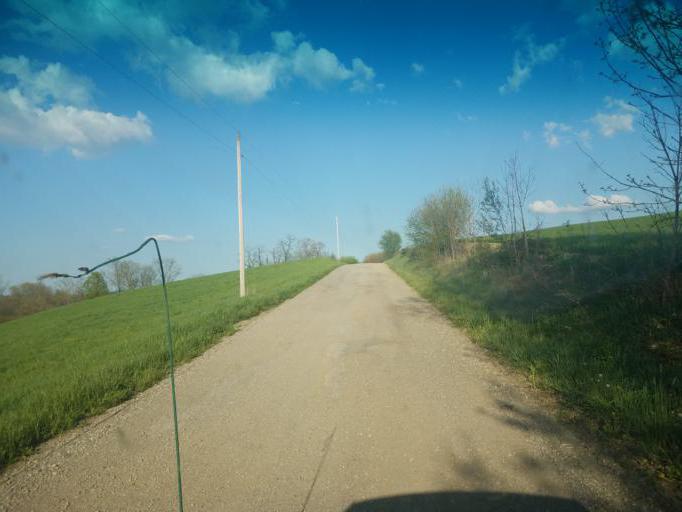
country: US
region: Ohio
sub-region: Wayne County
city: Shreve
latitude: 40.5950
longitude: -82.0574
